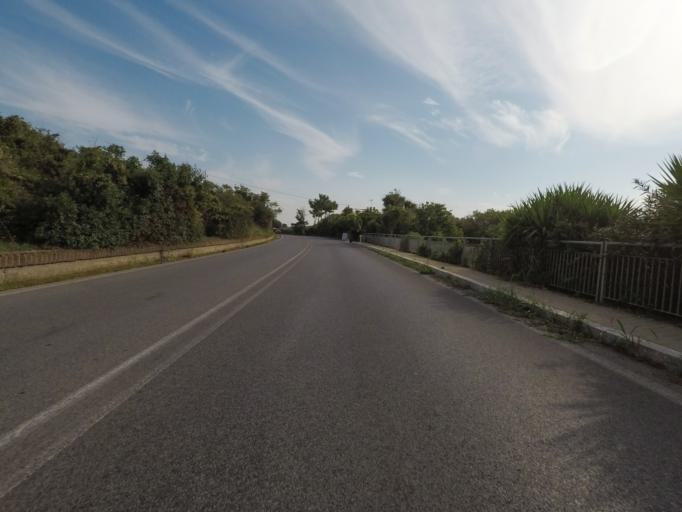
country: IT
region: Latium
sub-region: Citta metropolitana di Roma Capitale
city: Civitavecchia
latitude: 42.0645
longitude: 11.8140
